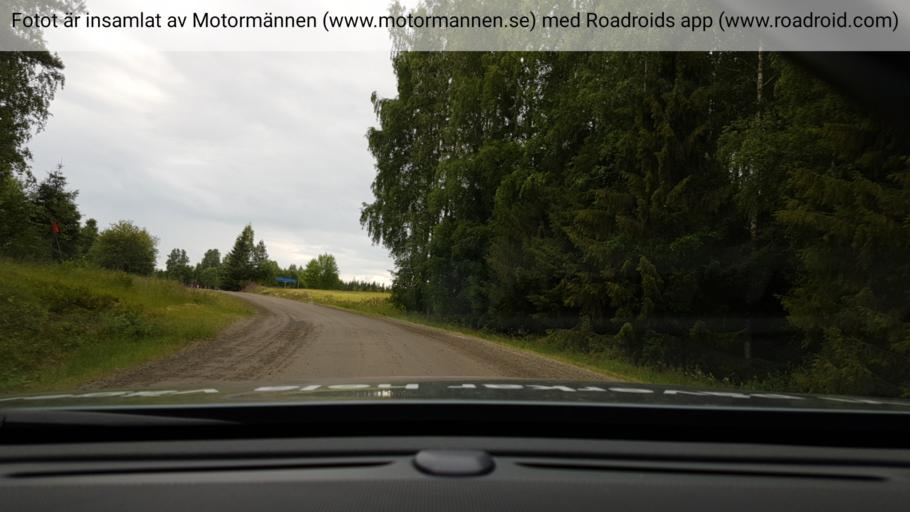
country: SE
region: Vaesterbotten
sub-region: Vannas Kommun
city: Vannasby
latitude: 64.0997
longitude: 20.0464
